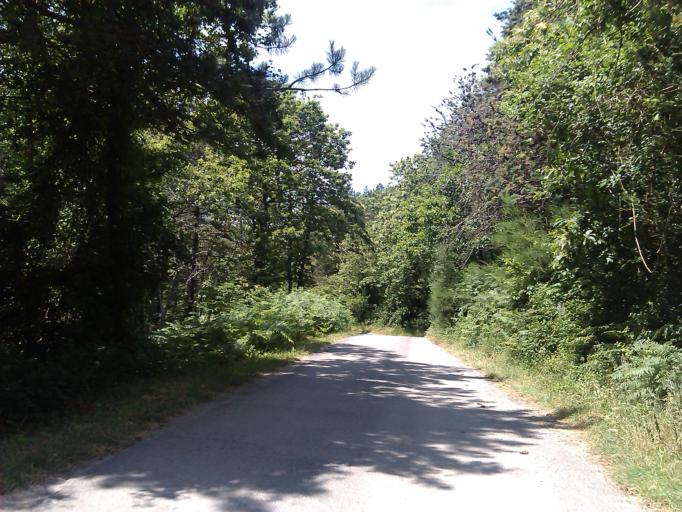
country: IT
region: Tuscany
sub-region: Provincia di Pistoia
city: Montale
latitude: 43.9749
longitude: 11.0379
